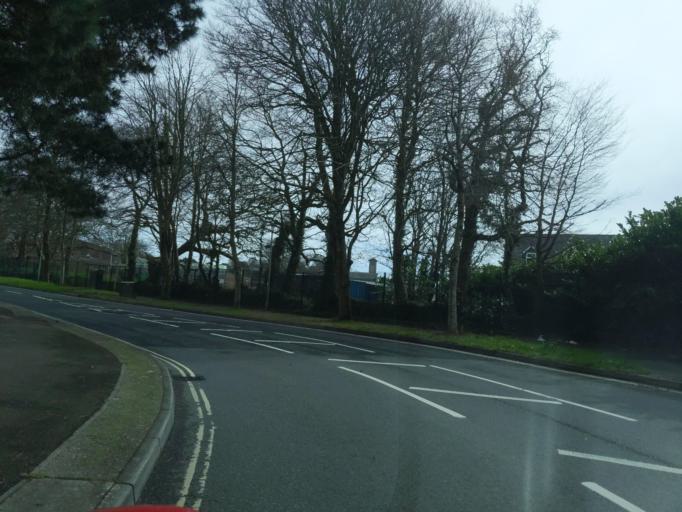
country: GB
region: England
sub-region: Plymouth
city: Plymouth
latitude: 50.4070
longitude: -4.1383
